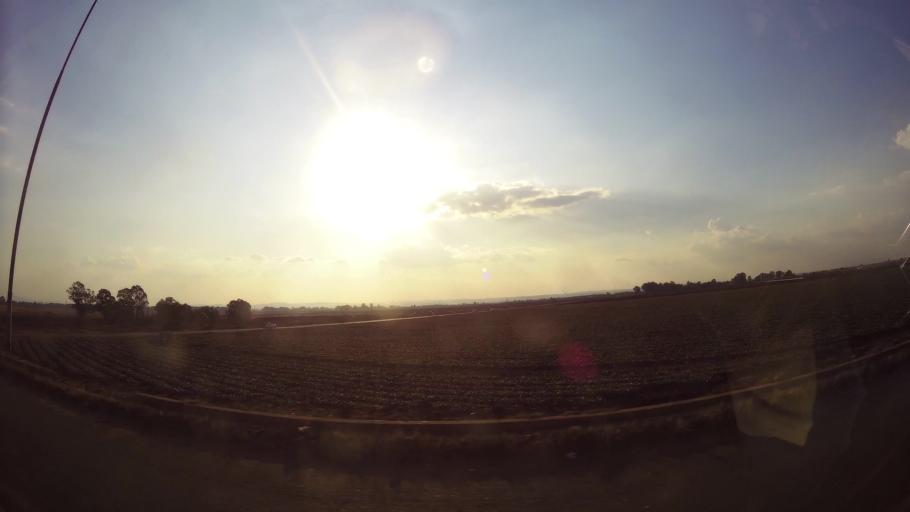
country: ZA
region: Gauteng
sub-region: Ekurhuleni Metropolitan Municipality
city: Germiston
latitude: -26.3277
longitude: 28.2390
